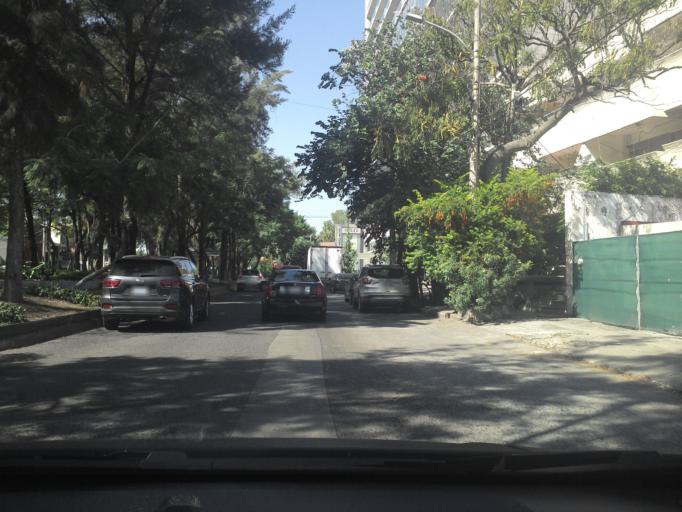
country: MX
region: Jalisco
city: Zapopan2
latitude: 20.6979
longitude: -103.3836
